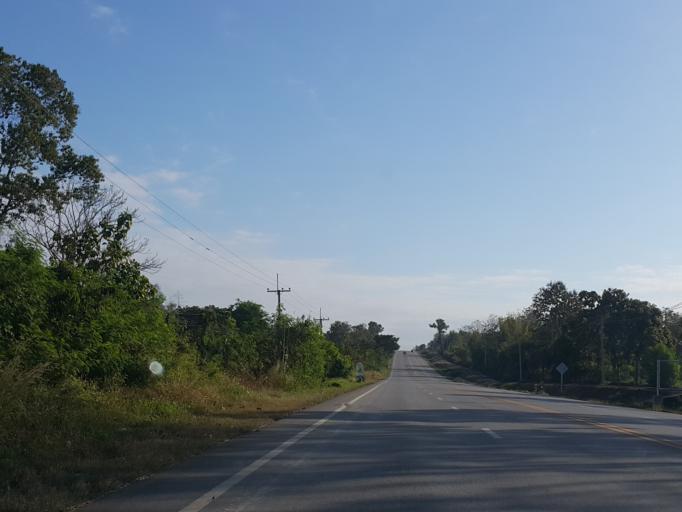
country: TH
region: Lampang
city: Mae Mo
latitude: 18.2575
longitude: 99.6152
